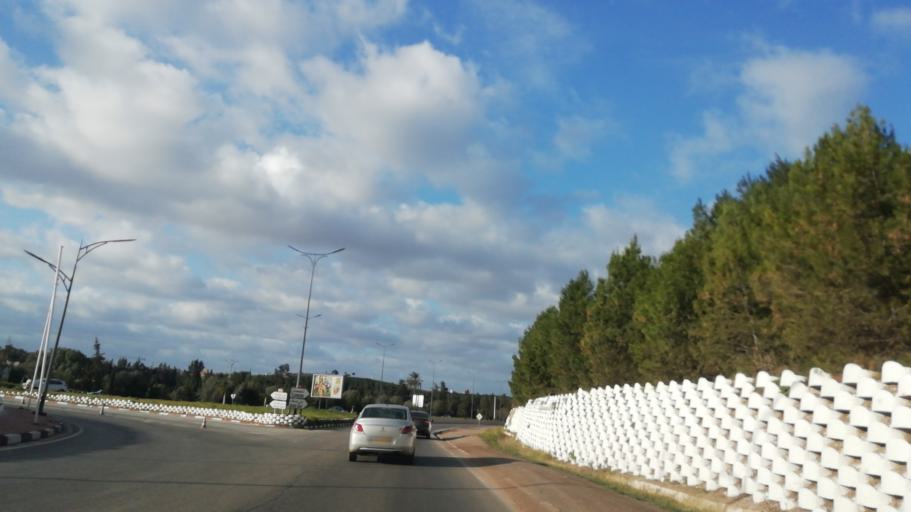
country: DZ
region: Ain Temouchent
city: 'Ain Temouchent
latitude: 35.3264
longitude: -1.1244
